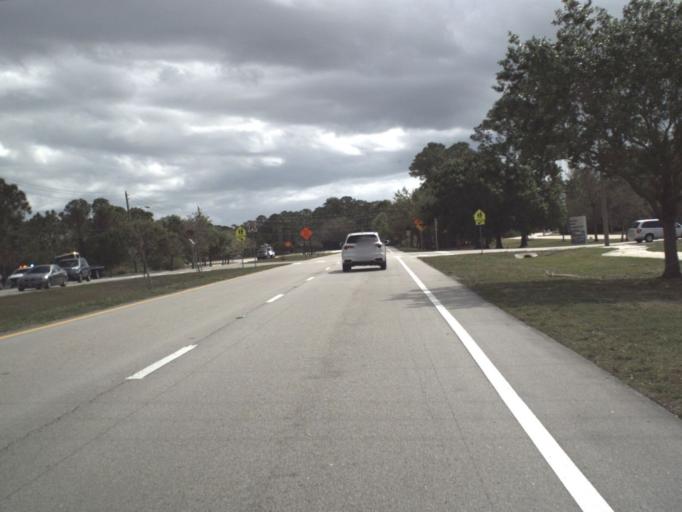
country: US
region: Florida
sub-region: Saint Lucie County
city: White City
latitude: 27.3626
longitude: -80.3548
